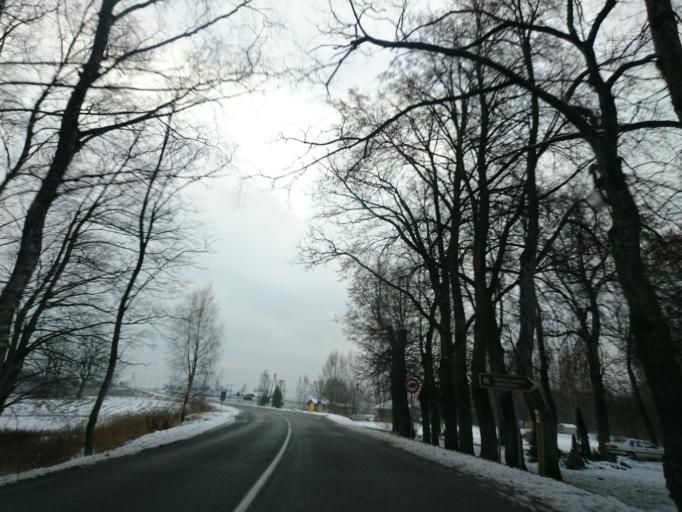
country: LV
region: Seja
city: Loja
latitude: 57.1650
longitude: 24.6210
